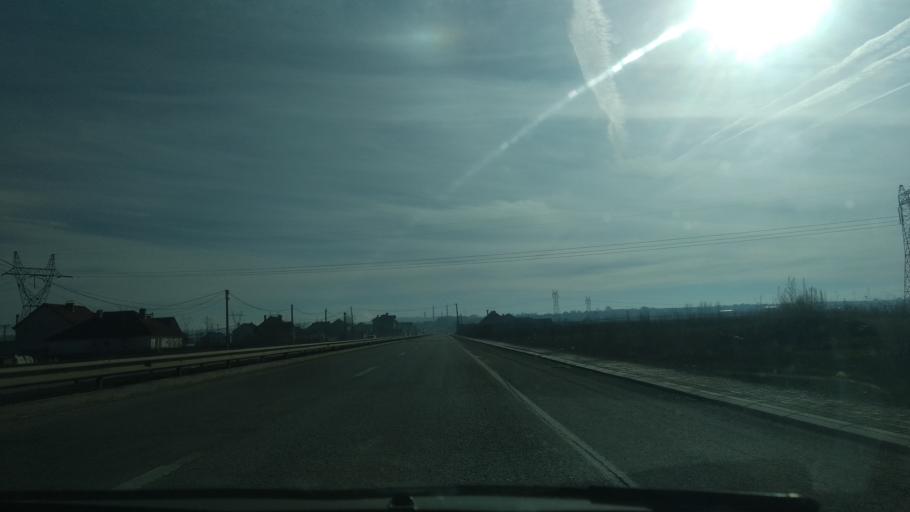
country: XK
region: Pristina
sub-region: Komuna e Obiliqit
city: Obiliq
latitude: 42.7104
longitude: 21.1018
